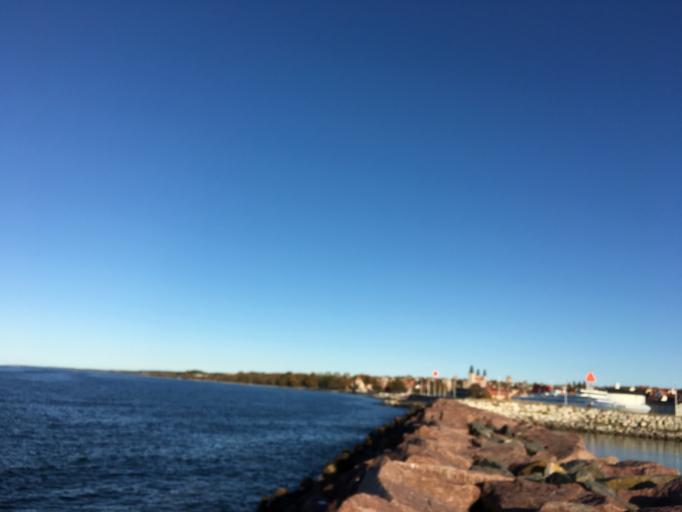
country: SE
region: Gotland
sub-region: Gotland
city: Visby
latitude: 57.6378
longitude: 18.2775
